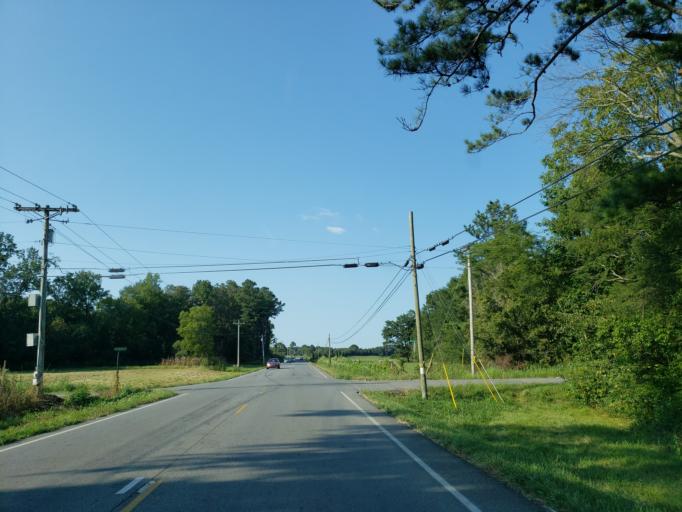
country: US
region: Tennessee
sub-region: Bradley County
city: Wildwood Lake
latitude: 35.0139
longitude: -84.7336
